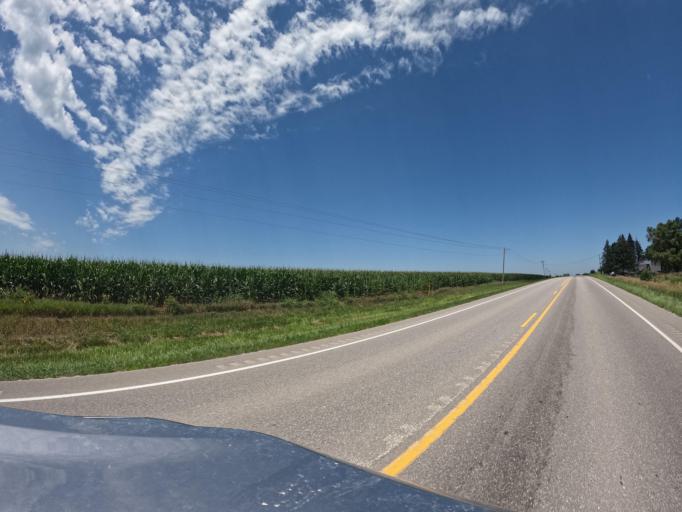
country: US
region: Iowa
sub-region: Keokuk County
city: Sigourney
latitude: 41.4145
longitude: -92.3548
